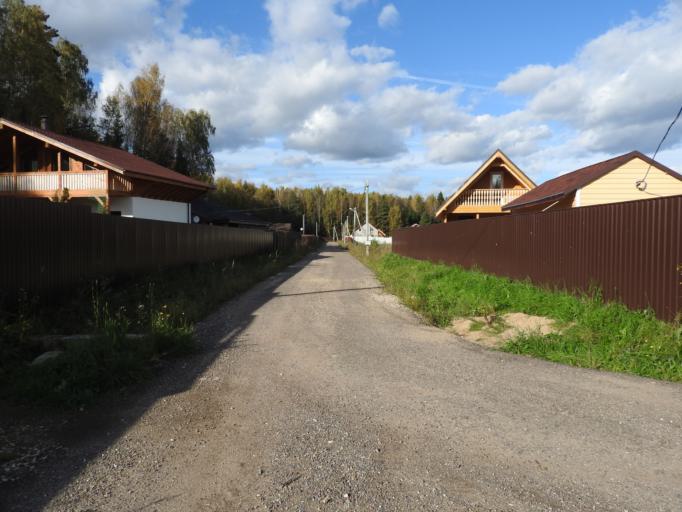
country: RU
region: Moskovskaya
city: Ruza
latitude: 55.5315
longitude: 36.1999
